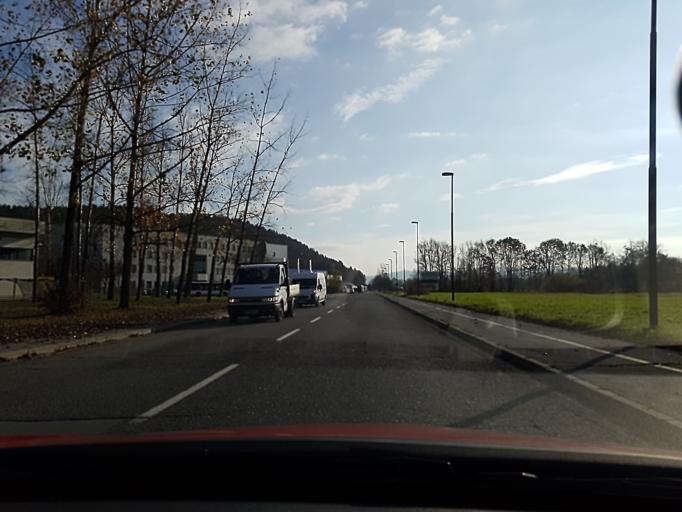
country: SI
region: Trzin
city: Trzin
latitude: 46.0936
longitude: 14.5545
